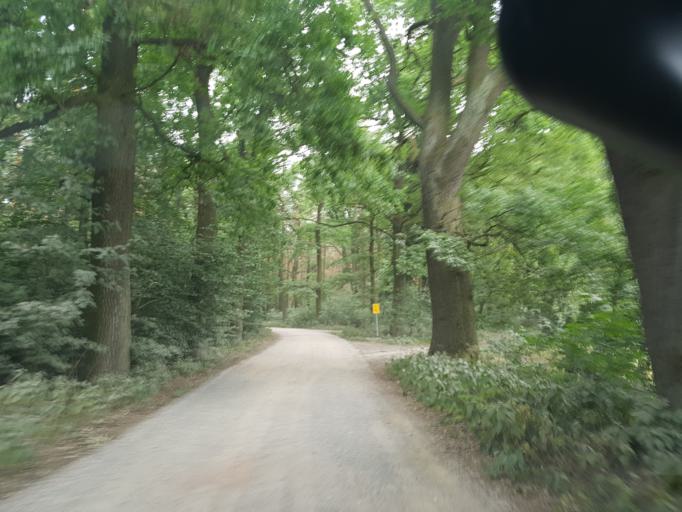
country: DE
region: Brandenburg
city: Schonewalde
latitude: 51.7021
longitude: 13.5345
